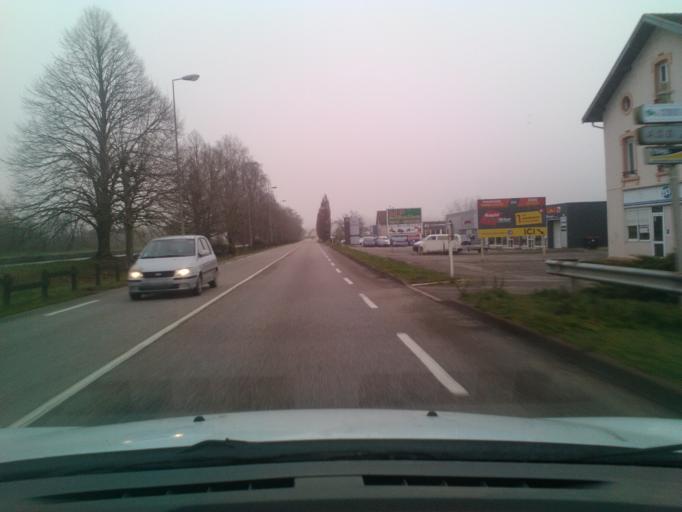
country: FR
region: Lorraine
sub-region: Departement des Vosges
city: Chavelot
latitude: 48.2205
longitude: 6.4368
